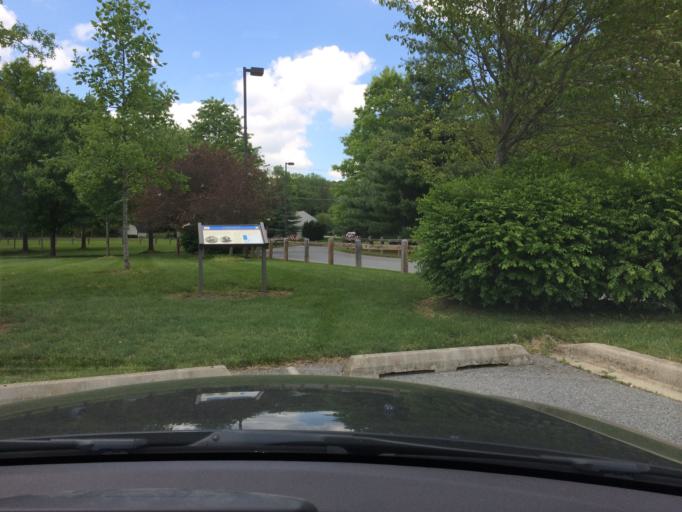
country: US
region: Maryland
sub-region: Frederick County
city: Linganore
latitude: 39.4837
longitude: -77.2363
